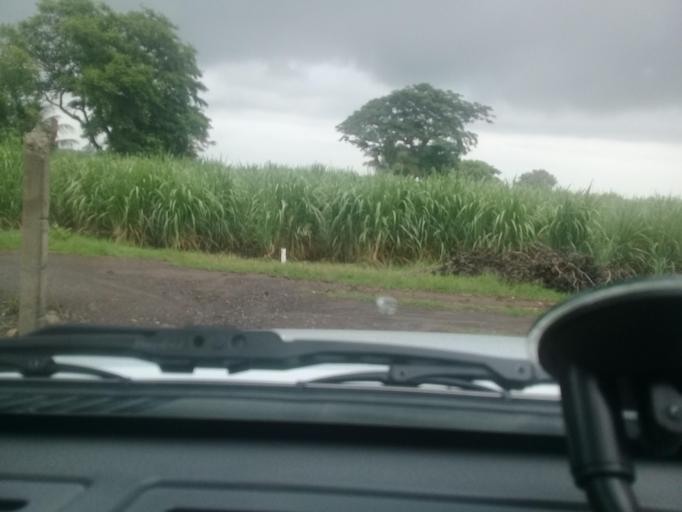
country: MX
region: Veracruz
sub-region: La Antigua
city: Nicolas Blanco (San Pancho)
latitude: 19.3367
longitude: -96.3604
